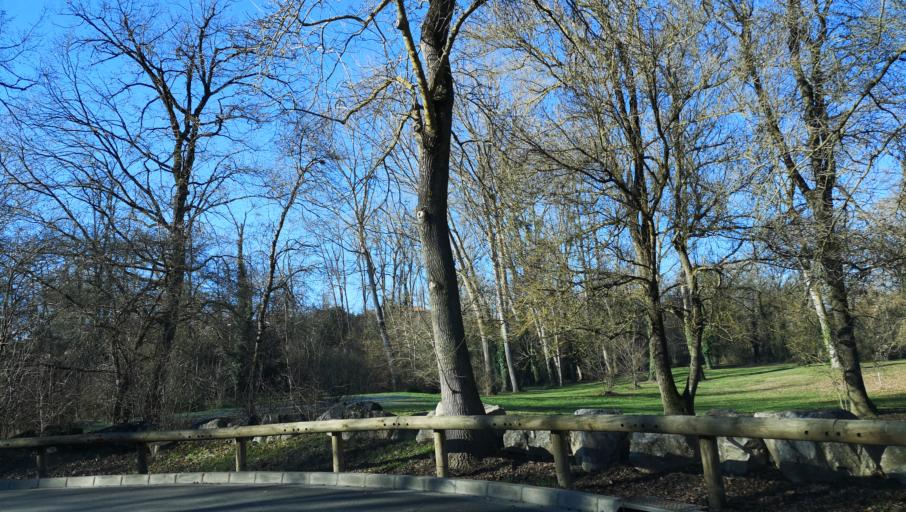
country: FR
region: Midi-Pyrenees
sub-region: Departement de la Haute-Garonne
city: Beauzelle
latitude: 43.6626
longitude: 1.3919
